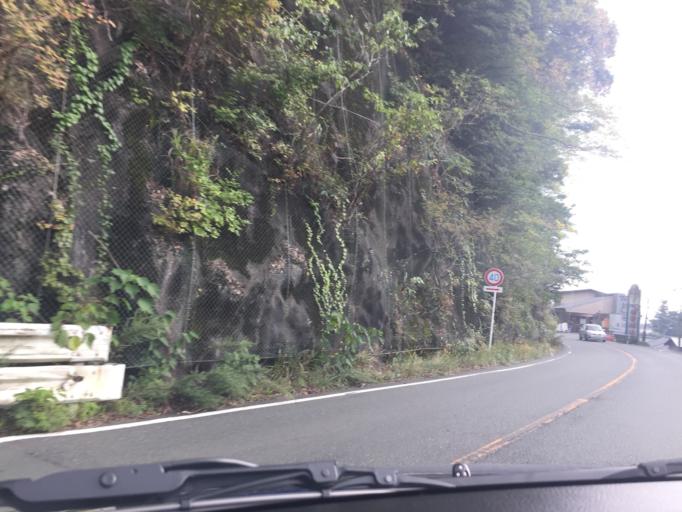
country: JP
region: Aichi
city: Shinshiro
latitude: 34.9657
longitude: 137.6136
